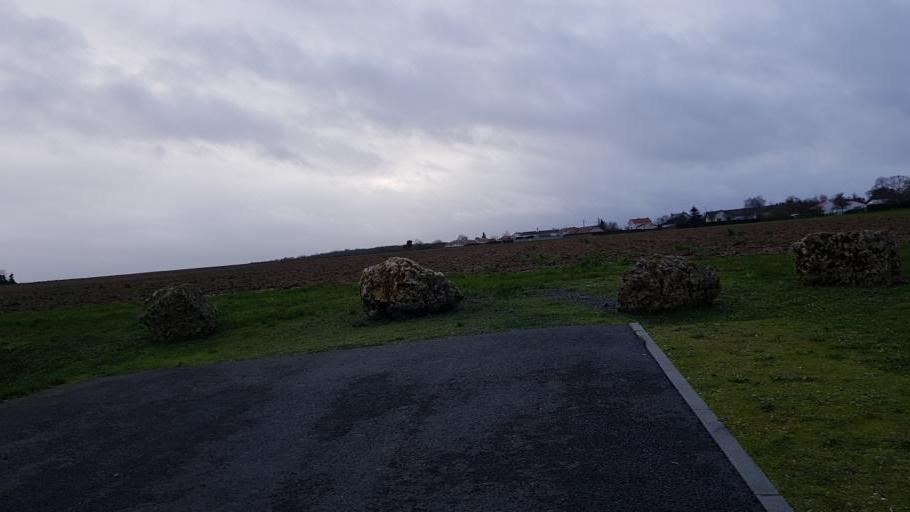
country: FR
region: Poitou-Charentes
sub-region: Departement de la Vienne
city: Avanton
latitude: 46.6613
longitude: 0.3091
